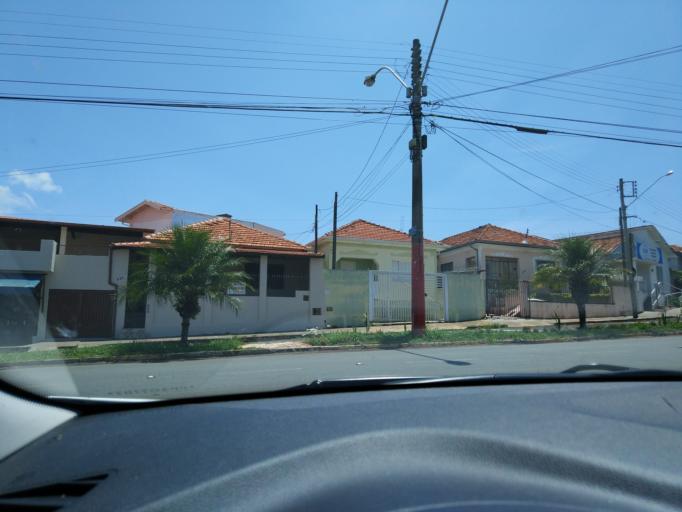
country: BR
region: Sao Paulo
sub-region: Botucatu
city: Botucatu
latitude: -22.8681
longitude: -48.4433
